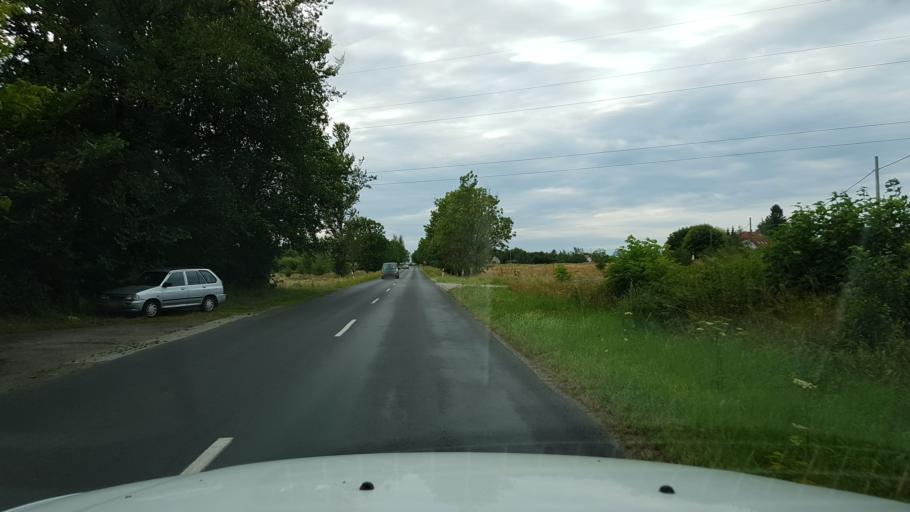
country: PL
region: West Pomeranian Voivodeship
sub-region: Powiat kolobrzeski
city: Kolobrzeg
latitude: 54.1503
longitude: 15.6371
